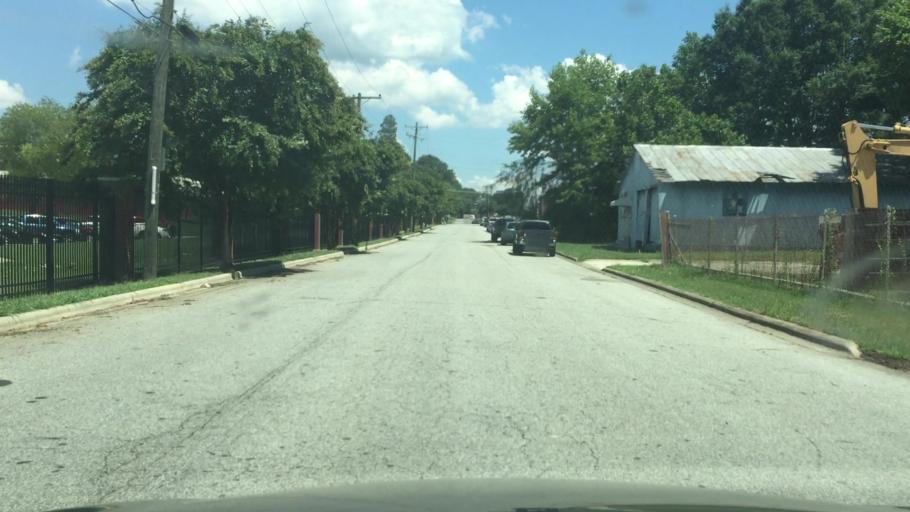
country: US
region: North Carolina
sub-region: Rowan County
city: Salisbury
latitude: 35.6812
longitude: -80.4900
